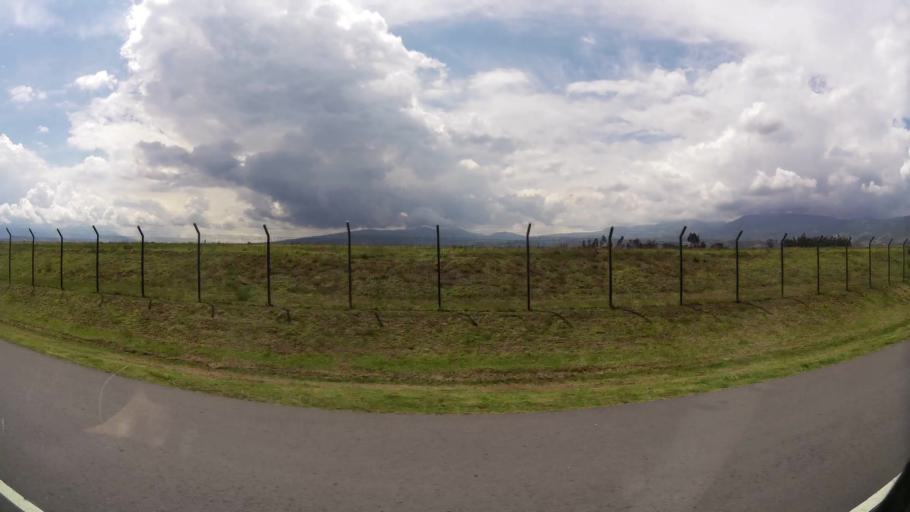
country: EC
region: Pichincha
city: Quito
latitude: -0.1474
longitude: -78.3542
